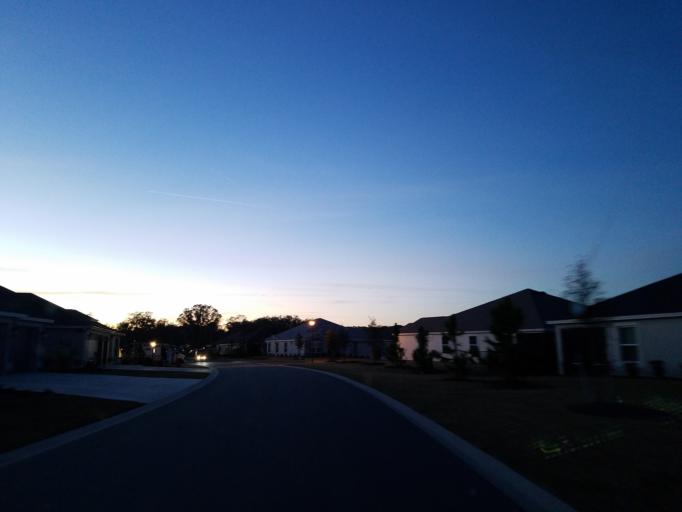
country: US
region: Florida
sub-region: Sumter County
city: Wildwood
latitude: 28.7979
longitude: -82.0347
